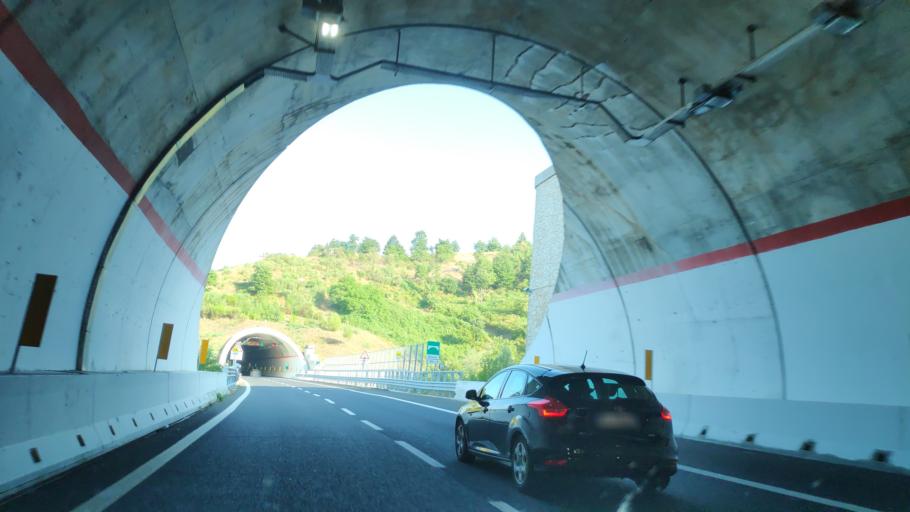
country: IT
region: Basilicate
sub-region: Provincia di Potenza
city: Lagonegro
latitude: 40.1101
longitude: 15.7926
